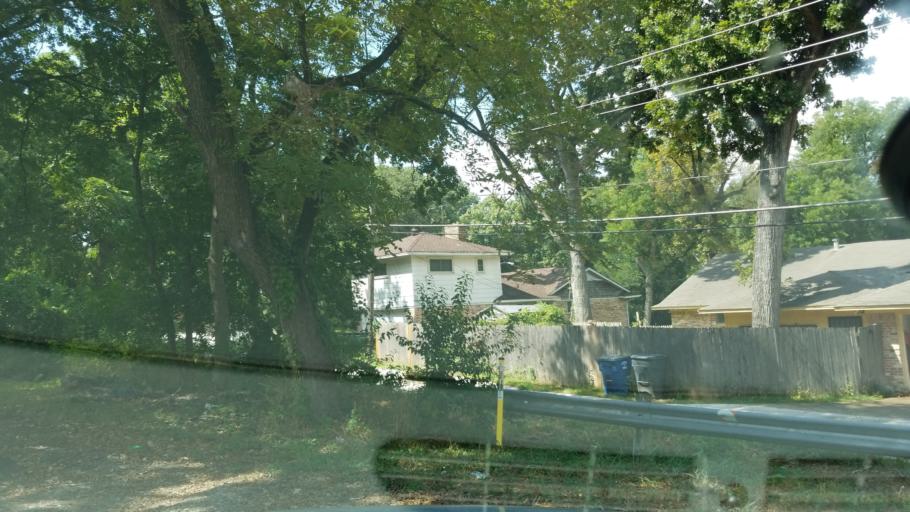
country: US
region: Texas
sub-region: Dallas County
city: Duncanville
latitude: 32.6712
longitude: -96.8354
